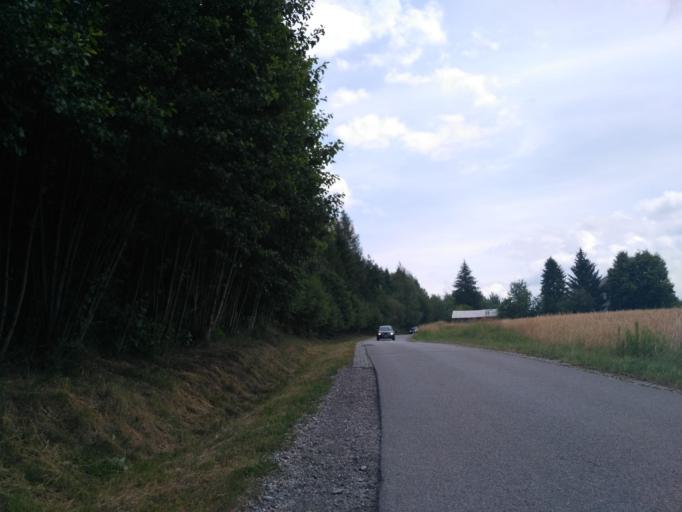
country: PL
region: Subcarpathian Voivodeship
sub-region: Powiat ropczycko-sedziszowski
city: Niedzwiada
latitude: 50.0367
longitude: 21.5003
